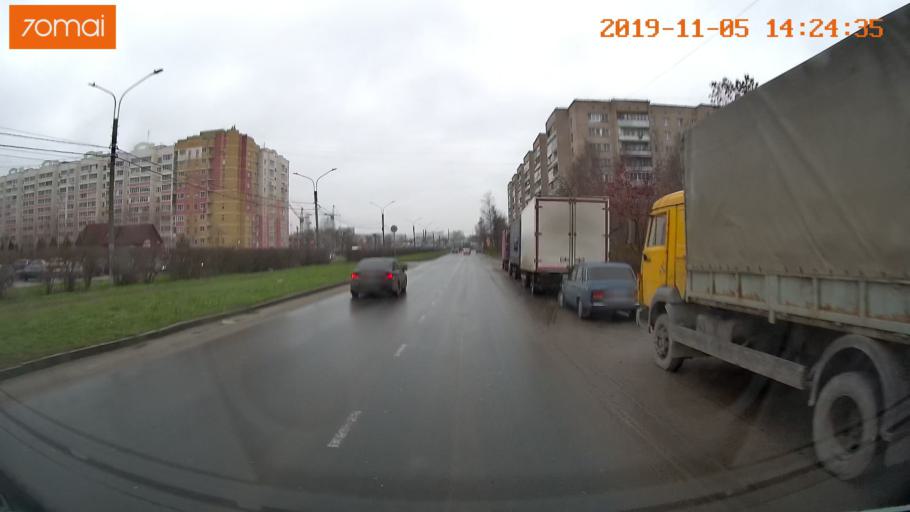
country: RU
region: Ivanovo
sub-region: Gorod Ivanovo
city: Ivanovo
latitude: 56.9690
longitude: 40.9967
